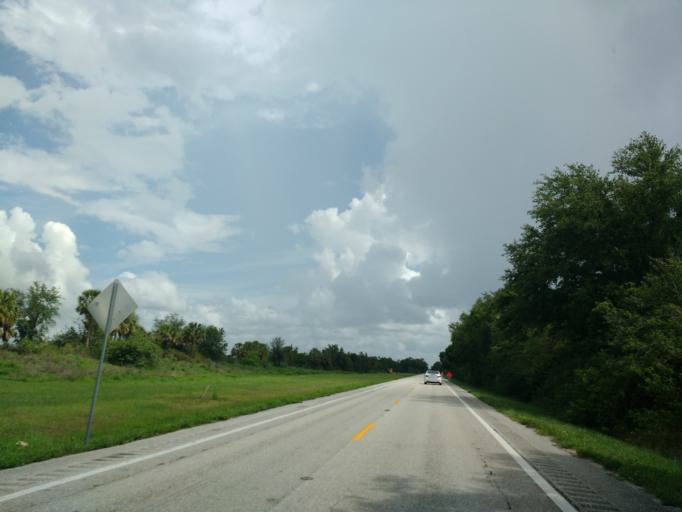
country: US
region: Florida
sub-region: Lee County
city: Burnt Store Marina
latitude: 26.8248
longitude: -82.0215
